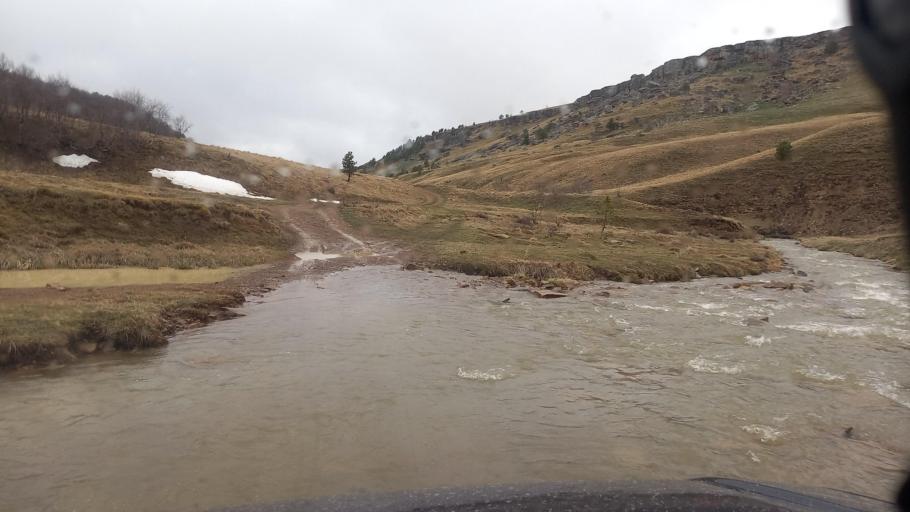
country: RU
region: Kabardino-Balkariya
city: Terskol
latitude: 43.5236
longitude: 42.4277
